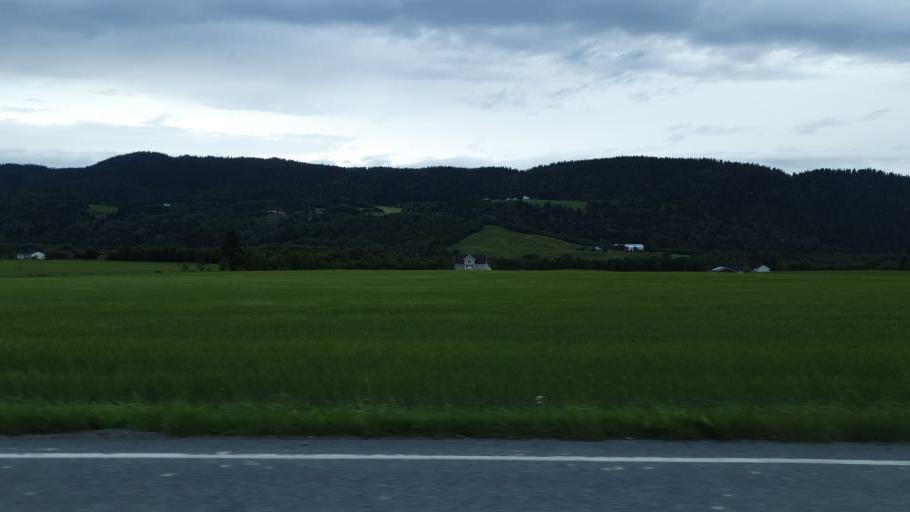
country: NO
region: Sor-Trondelag
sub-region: Melhus
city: Lundamo
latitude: 63.1735
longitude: 10.3164
